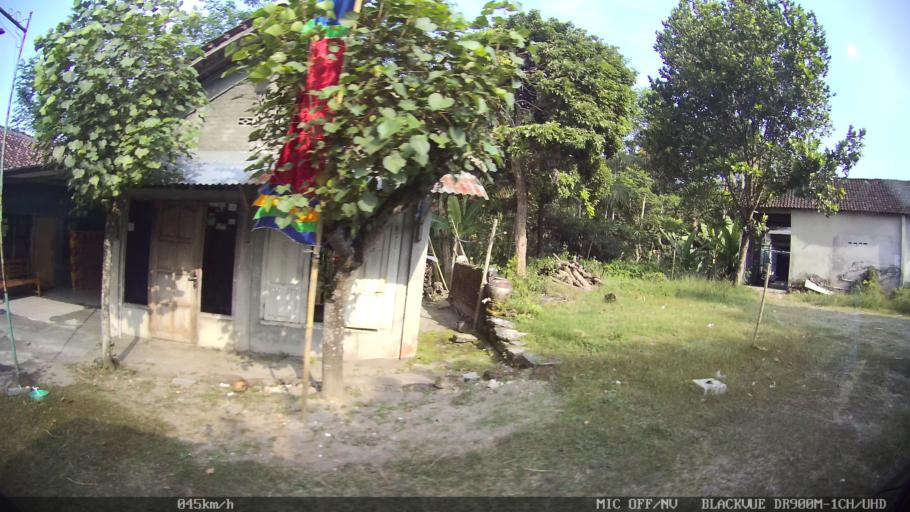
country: ID
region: Daerah Istimewa Yogyakarta
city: Bantul
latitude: -7.8710
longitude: 110.3169
